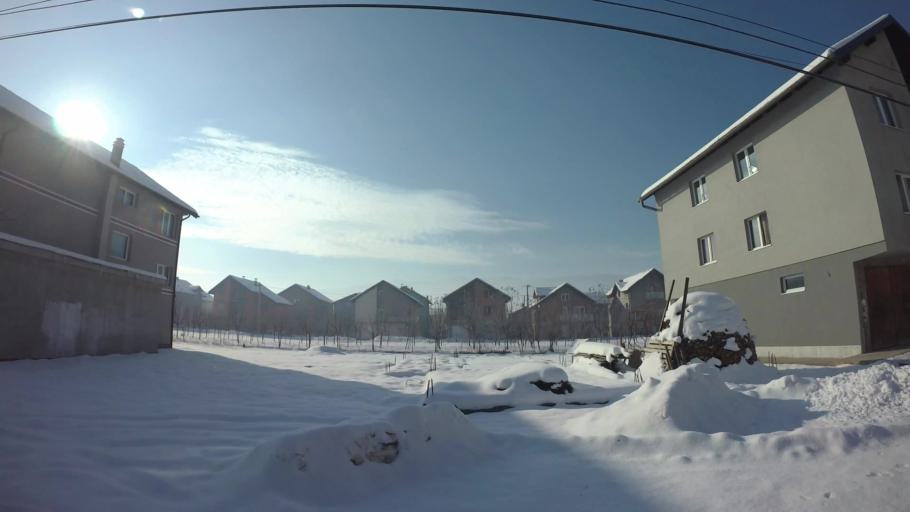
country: BA
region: Federation of Bosnia and Herzegovina
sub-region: Kanton Sarajevo
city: Sarajevo
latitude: 43.8298
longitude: 18.3276
